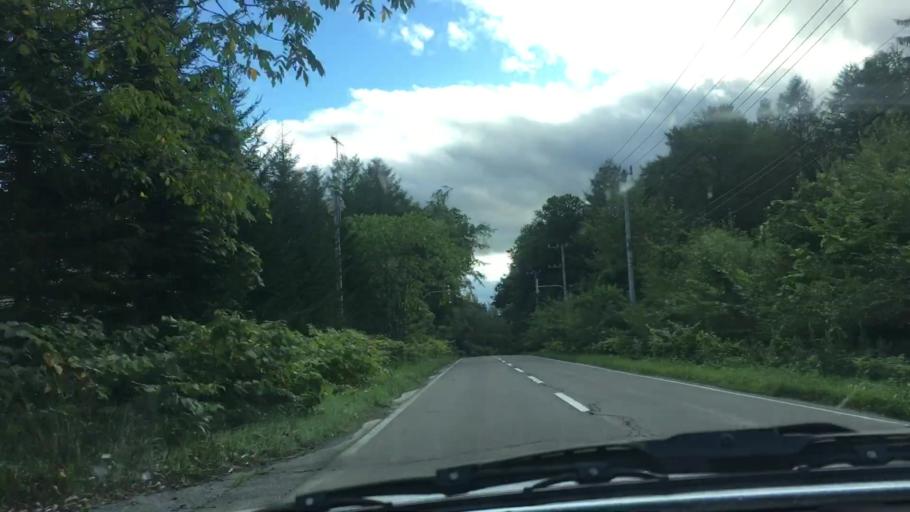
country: JP
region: Hokkaido
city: Otofuke
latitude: 43.1701
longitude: 142.9125
